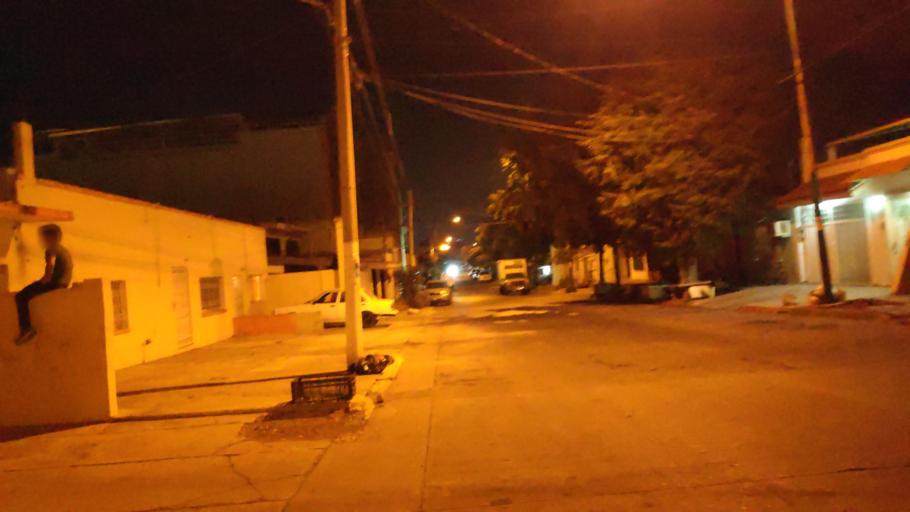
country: MX
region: Sinaloa
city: Culiacan
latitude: 24.7918
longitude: -107.4118
